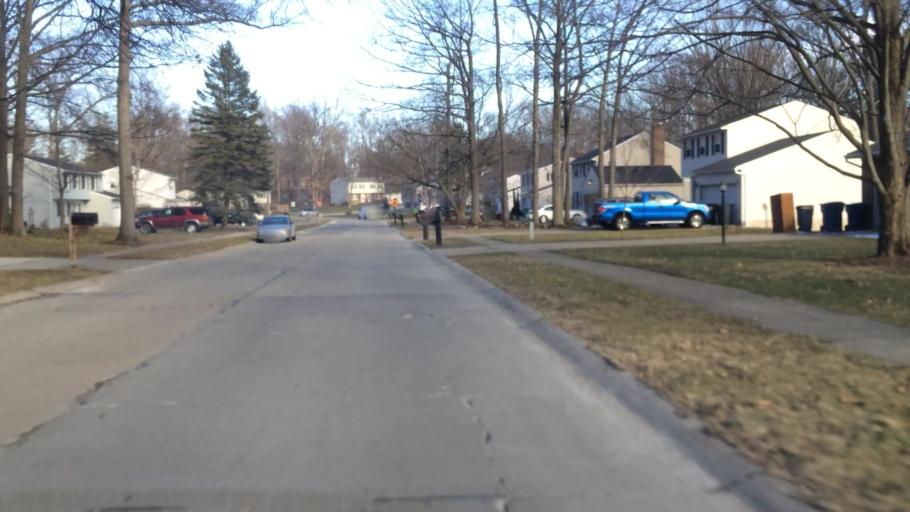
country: US
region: Ohio
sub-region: Summit County
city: Silver Lake
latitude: 41.1783
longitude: -81.4577
